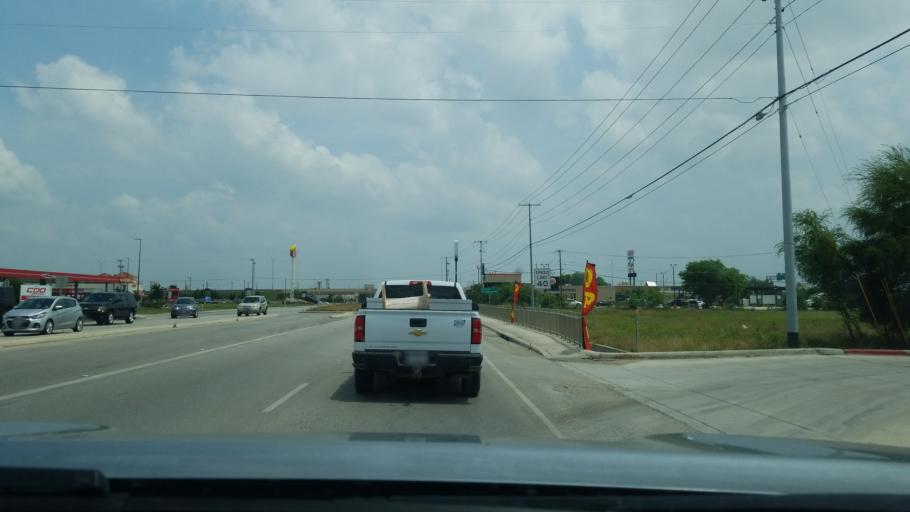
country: US
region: Texas
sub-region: Comal County
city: New Braunfels
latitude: 29.7310
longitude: -98.0809
